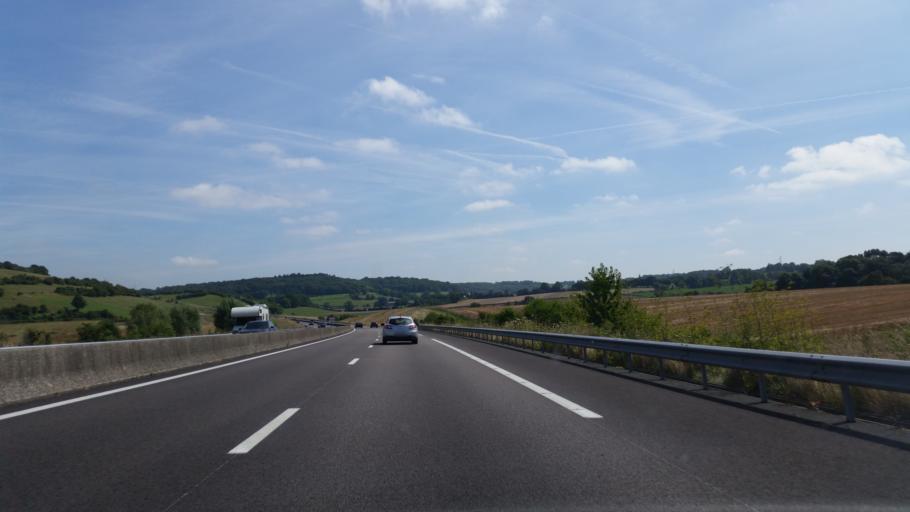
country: FR
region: Haute-Normandie
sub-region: Departement de la Seine-Maritime
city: Gaillefontaine
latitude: 49.7349
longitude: 1.5587
